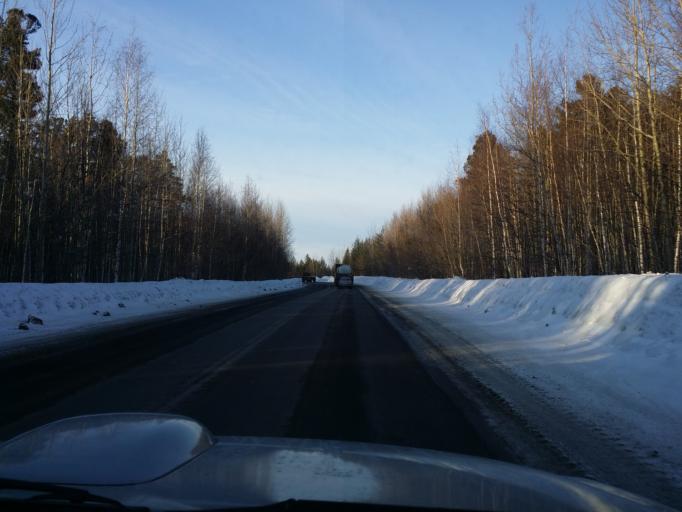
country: RU
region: Khanty-Mansiyskiy Avtonomnyy Okrug
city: Izluchinsk
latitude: 60.9592
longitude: 76.8509
